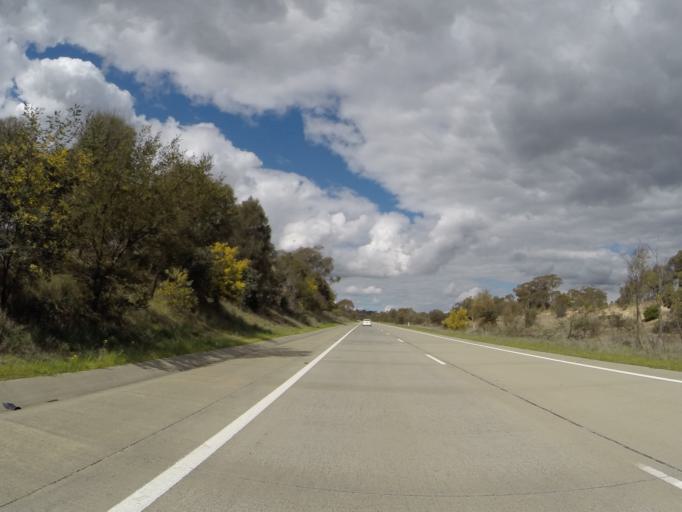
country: AU
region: New South Wales
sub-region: Yass Valley
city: Gundaroo
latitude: -34.7884
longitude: 149.2093
